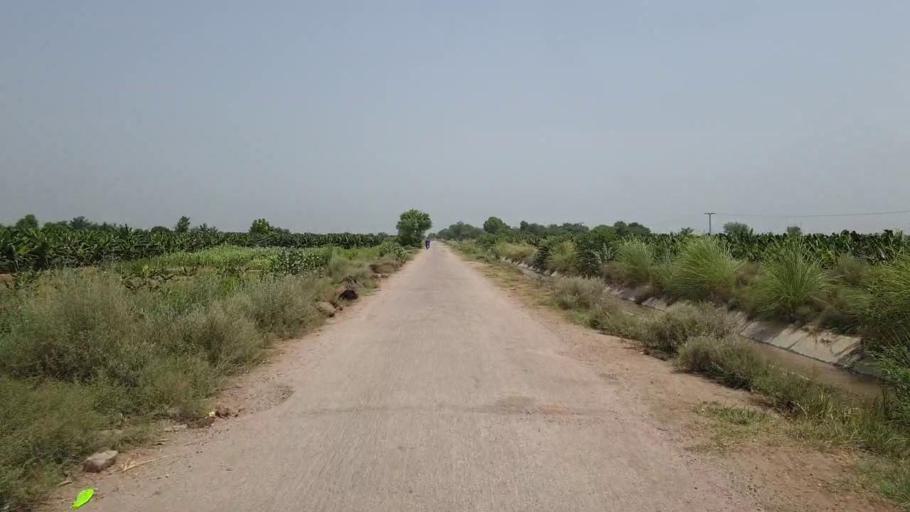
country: PK
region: Sindh
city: Nawabshah
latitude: 26.2834
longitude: 68.3111
